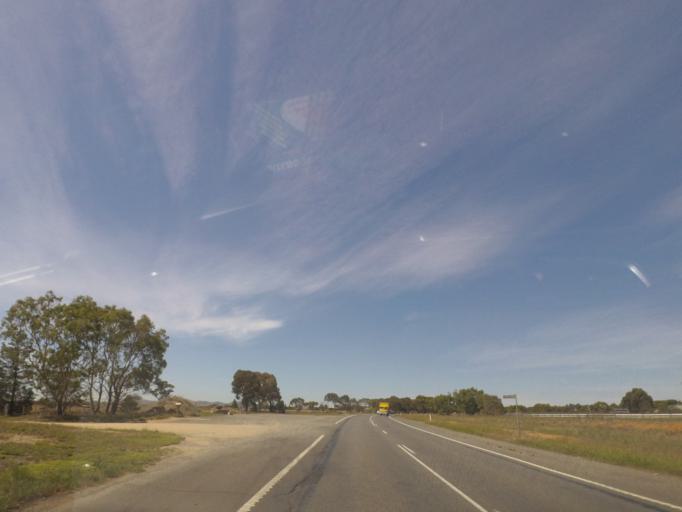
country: AU
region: Victoria
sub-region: Wyndham
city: Wyndham Vale
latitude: -37.8568
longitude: 144.3876
